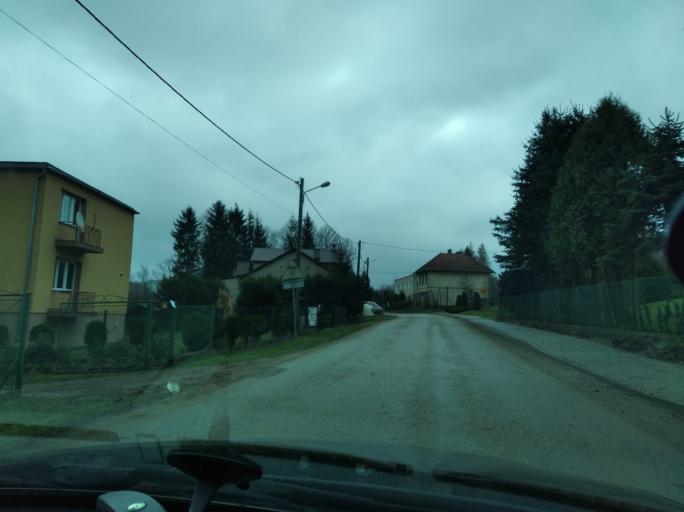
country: PL
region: Subcarpathian Voivodeship
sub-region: Powiat przeworski
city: Jawornik Polski
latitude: 49.9097
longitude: 22.2868
